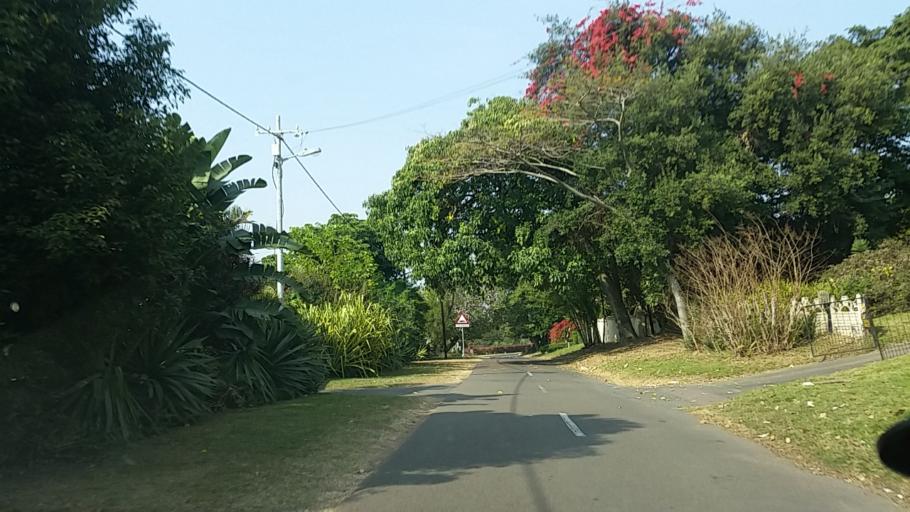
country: ZA
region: KwaZulu-Natal
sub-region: eThekwini Metropolitan Municipality
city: Berea
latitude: -29.8339
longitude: 30.9350
